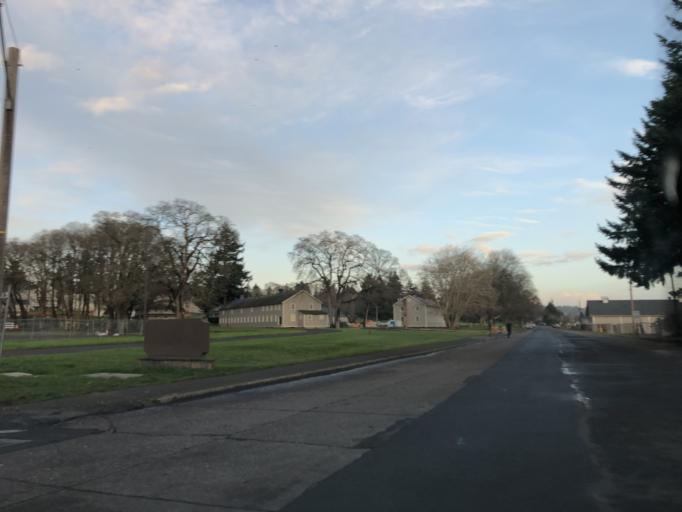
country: US
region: Washington
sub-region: Clark County
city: Vancouver
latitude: 45.6245
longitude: -122.6660
